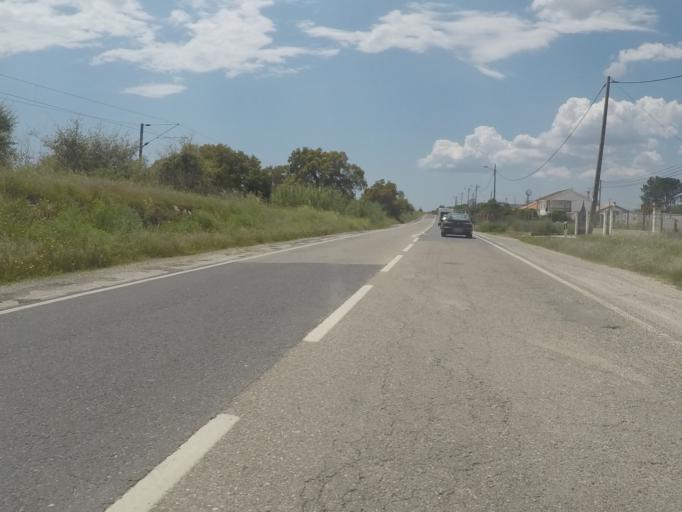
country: PT
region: Setubal
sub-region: Setubal
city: Setubal
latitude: 38.5590
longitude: -8.7914
